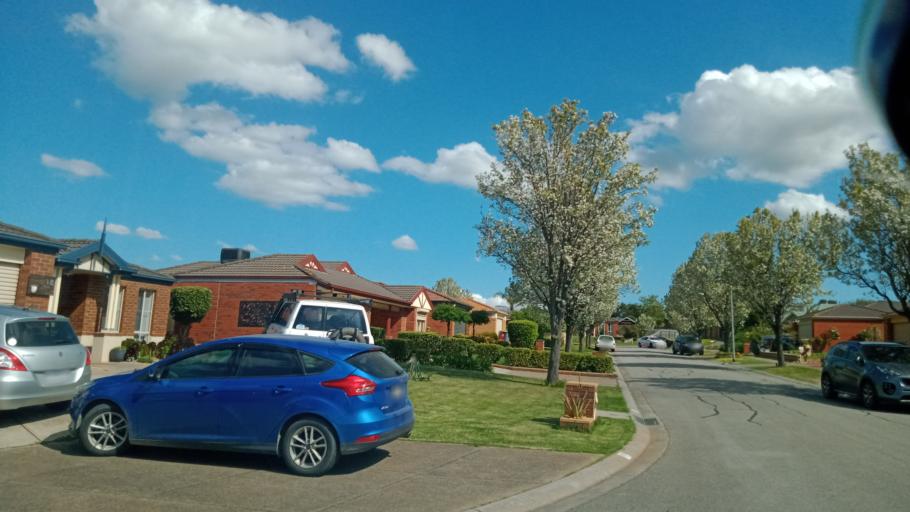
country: AU
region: Victoria
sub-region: Casey
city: Cranbourne West
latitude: -38.0961
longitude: 145.2620
